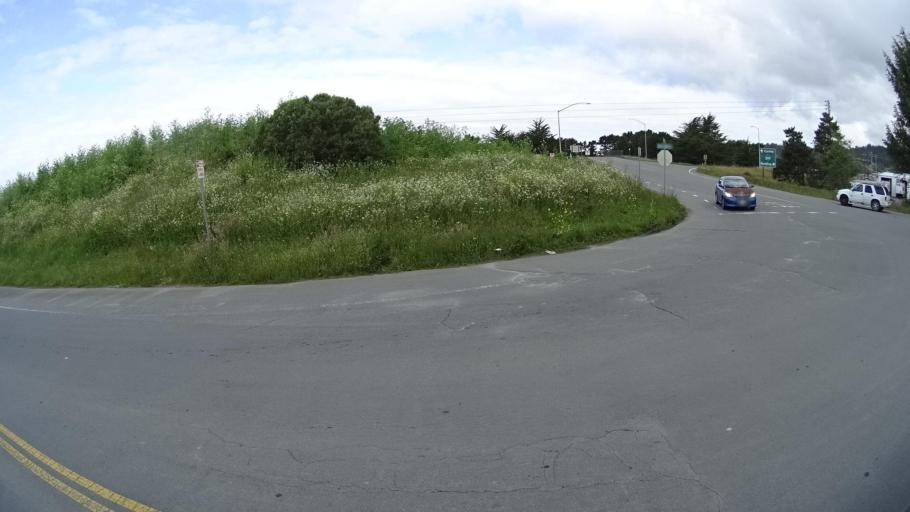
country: US
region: California
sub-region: Humboldt County
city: Arcata
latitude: 40.9032
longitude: -124.0720
